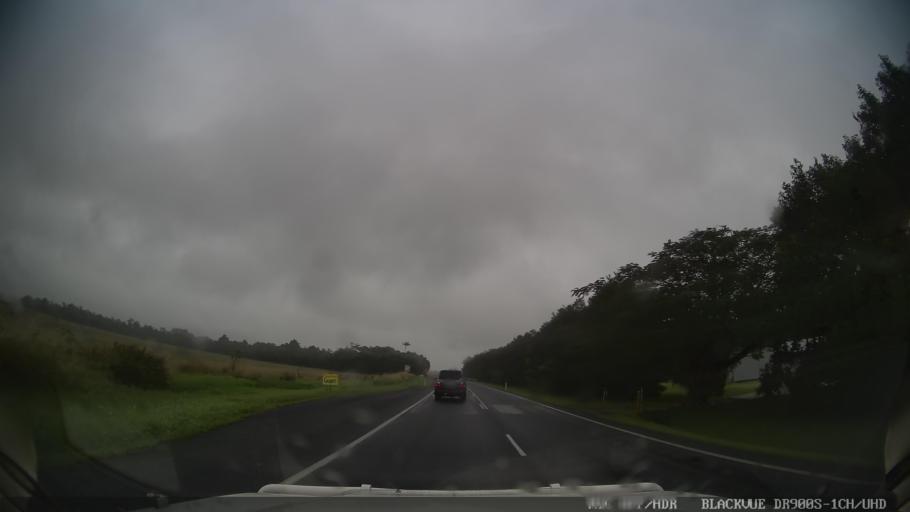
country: AU
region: Queensland
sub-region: Cassowary Coast
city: Innisfail
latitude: -17.6508
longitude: 146.0336
